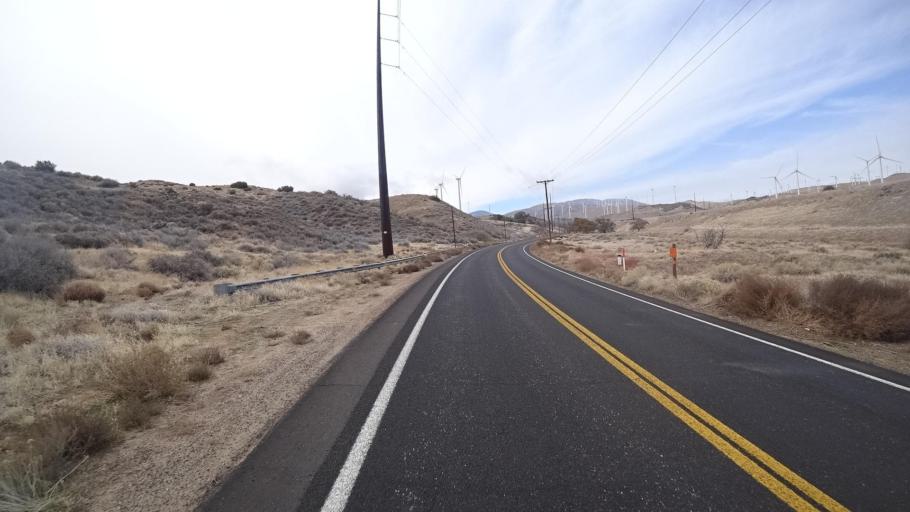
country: US
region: California
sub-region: Kern County
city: Tehachapi
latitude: 35.0504
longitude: -118.3495
